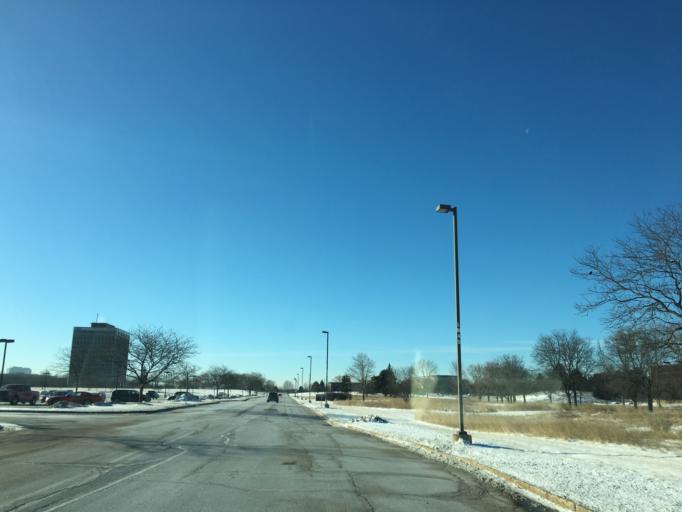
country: US
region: Illinois
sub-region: Cook County
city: Hoffman Estates
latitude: 42.0677
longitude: -88.0538
